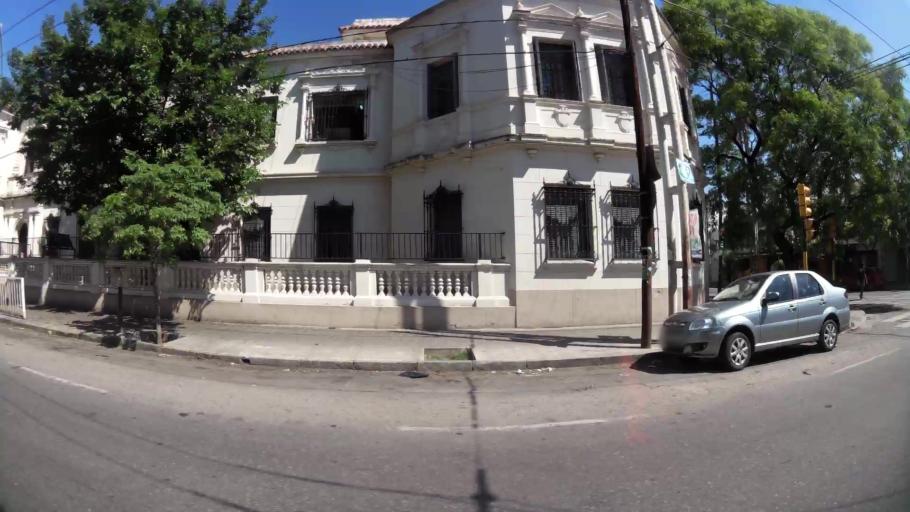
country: AR
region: Cordoba
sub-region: Departamento de Capital
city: Cordoba
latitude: -31.4134
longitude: -64.1644
